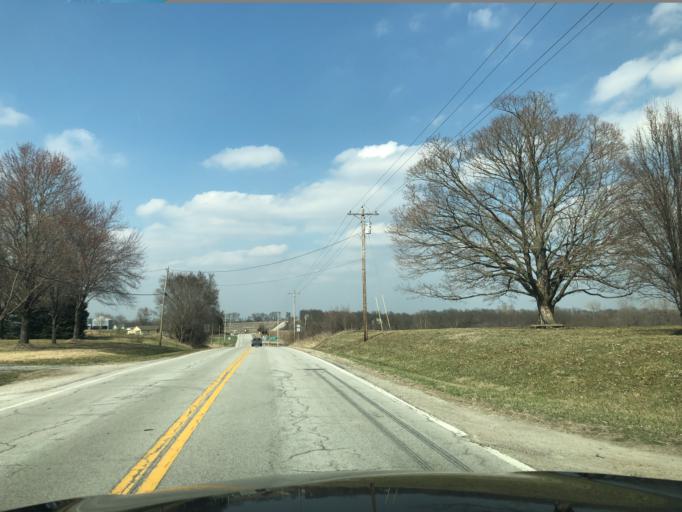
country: US
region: Missouri
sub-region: Platte County
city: Platte City
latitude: 39.4502
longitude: -94.8058
